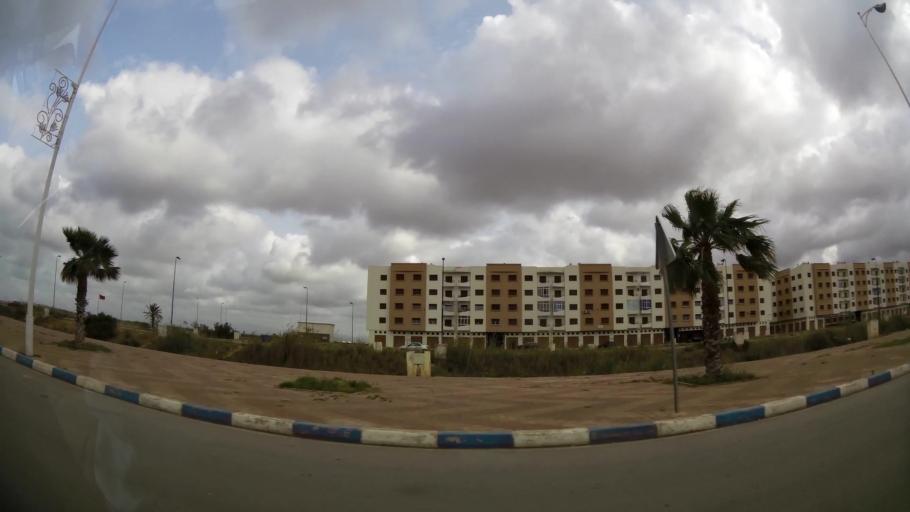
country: MA
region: Oriental
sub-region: Nador
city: Nador
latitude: 35.1537
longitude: -2.9082
